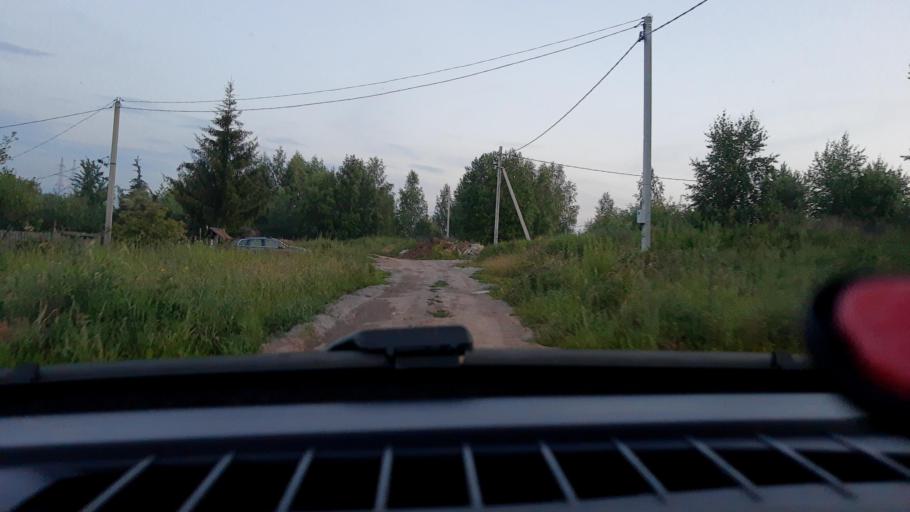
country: RU
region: Nizjnij Novgorod
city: Afonino
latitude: 56.2508
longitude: 44.0652
